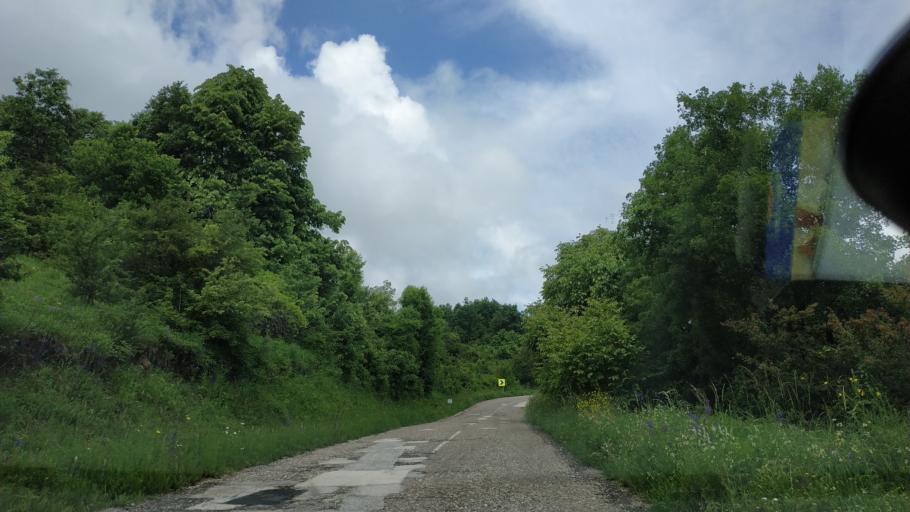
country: RS
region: Central Serbia
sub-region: Zajecarski Okrug
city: Boljevac
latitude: 43.7428
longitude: 21.9485
